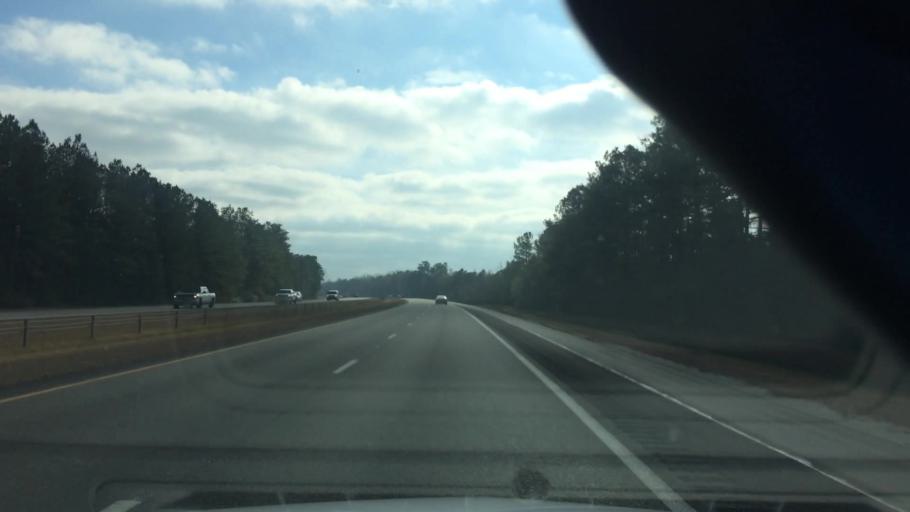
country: US
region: North Carolina
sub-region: Pender County
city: Rocky Point
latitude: 34.4662
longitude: -77.8802
